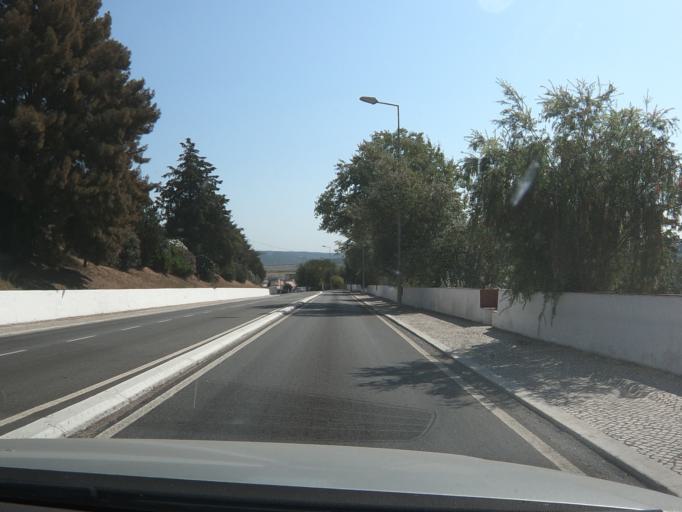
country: PT
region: Setubal
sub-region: Alcacer do Sal
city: Alcacer do Sal
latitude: 38.3740
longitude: -8.5088
